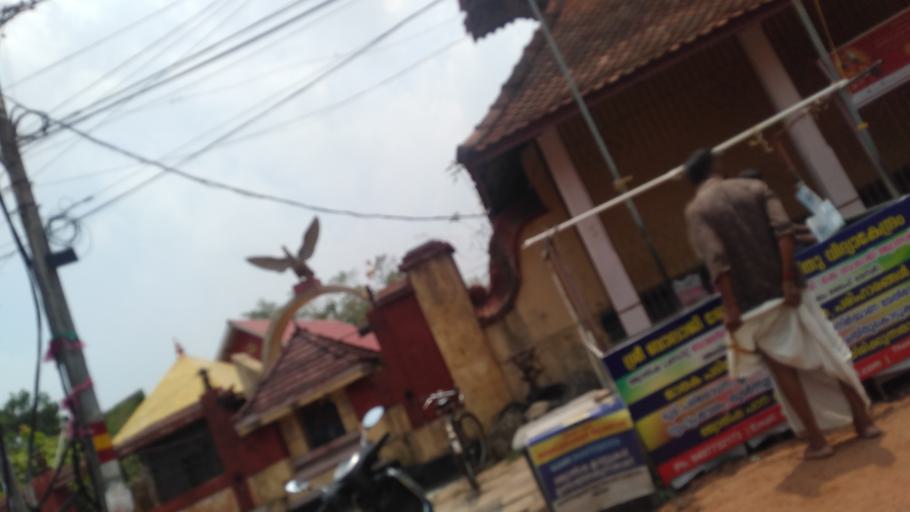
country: IN
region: Kerala
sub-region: Alappuzha
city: Alleppey
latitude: 9.4973
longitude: 76.3426
